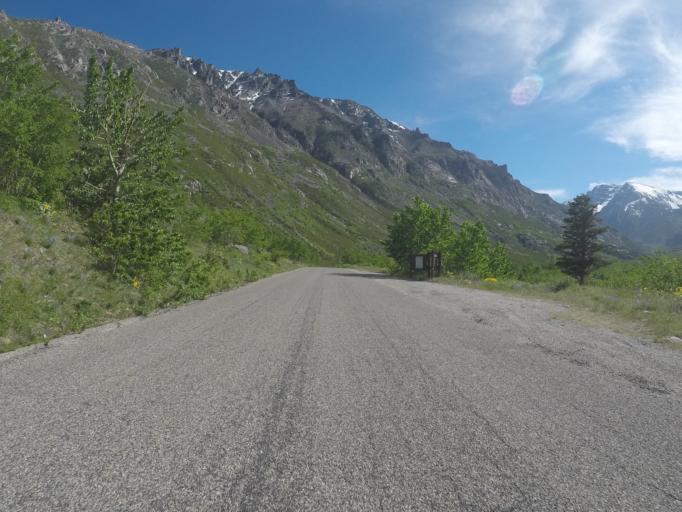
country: US
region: Montana
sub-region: Stillwater County
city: Absarokee
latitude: 45.2309
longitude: -109.6011
